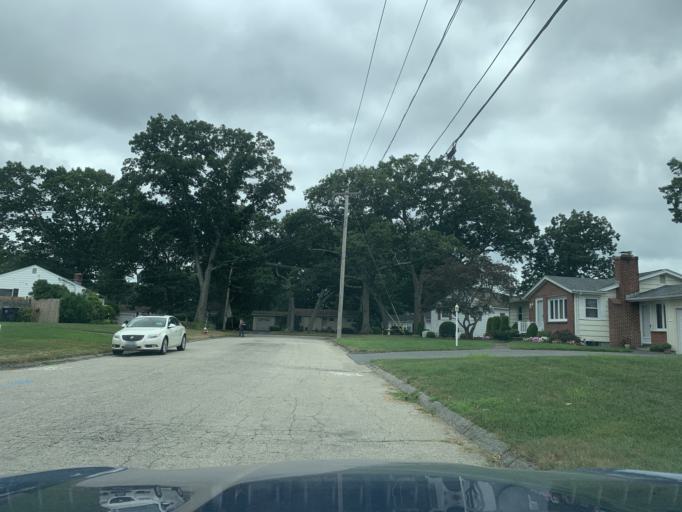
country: US
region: Rhode Island
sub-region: Kent County
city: Warwick
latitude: 41.7223
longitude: -71.4615
